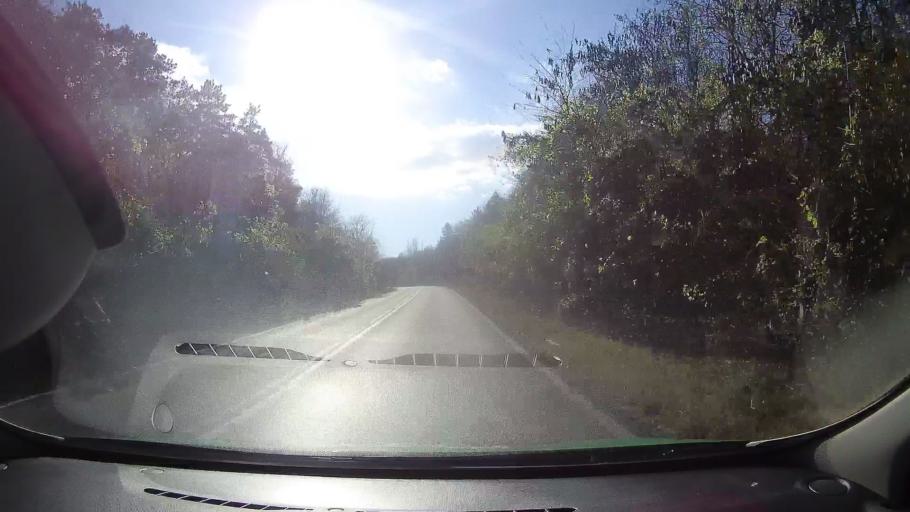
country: RO
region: Tulcea
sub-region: Oras Babadag
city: Babadag
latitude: 44.8712
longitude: 28.6885
